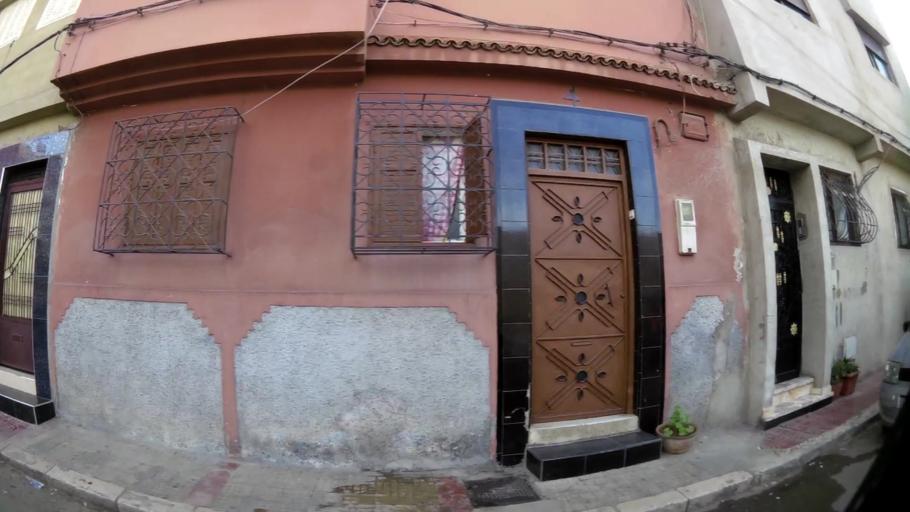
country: MA
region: Grand Casablanca
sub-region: Mohammedia
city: Mohammedia
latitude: 33.7006
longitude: -7.3835
